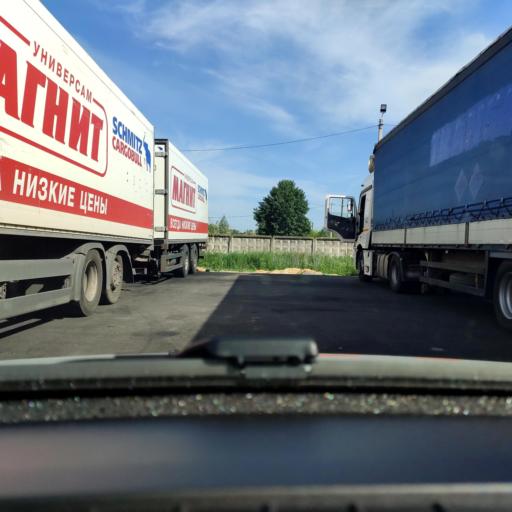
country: RU
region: Voronezj
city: Podgornoye
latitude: 51.8049
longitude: 39.2197
